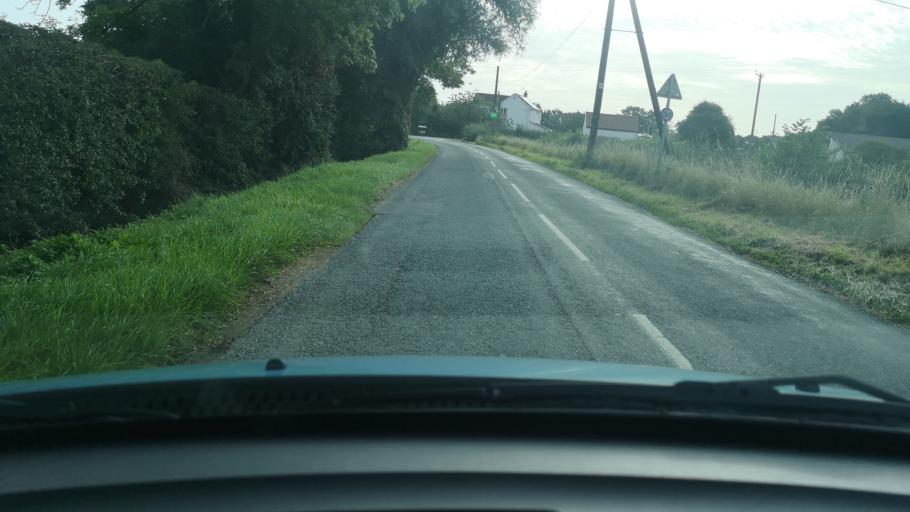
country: GB
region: England
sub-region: East Riding of Yorkshire
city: Pollington
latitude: 53.6395
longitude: -1.0580
